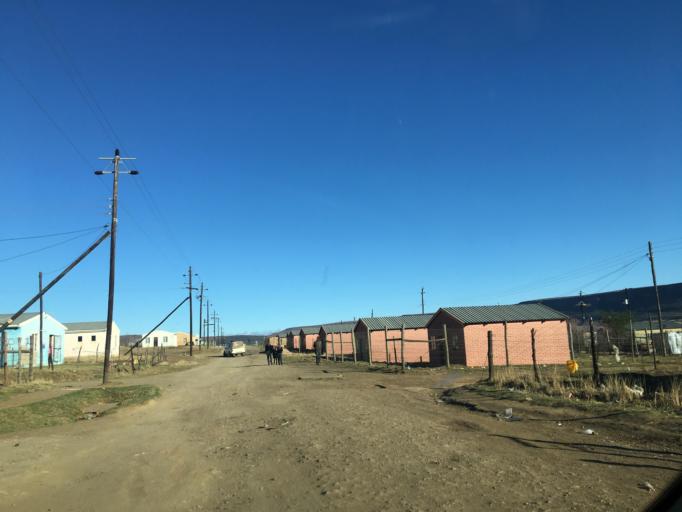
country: ZA
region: Eastern Cape
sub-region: Chris Hani District Municipality
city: Cala
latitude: -31.5406
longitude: 27.6838
